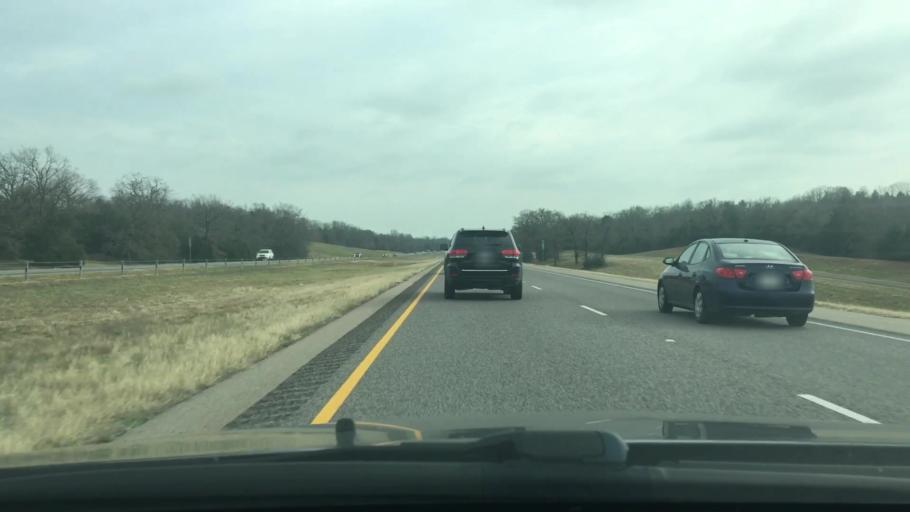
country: US
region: Texas
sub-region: Leon County
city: Buffalo
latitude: 31.5102
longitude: -96.1031
